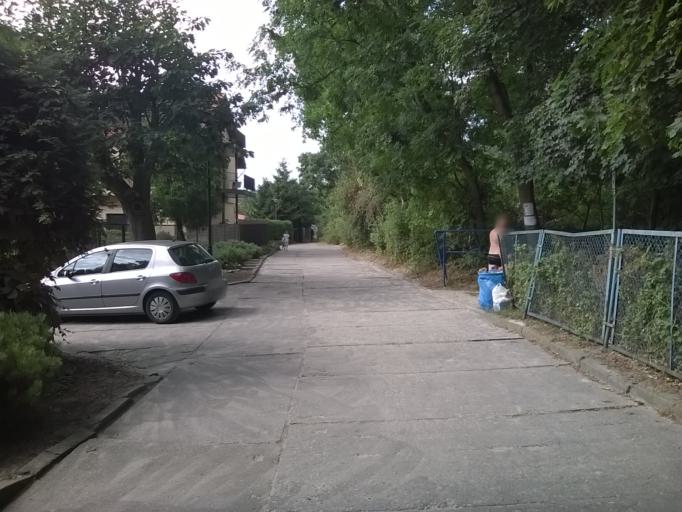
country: PL
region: West Pomeranian Voivodeship
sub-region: Powiat kolobrzeski
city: Ustronie Morskie
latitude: 54.2430
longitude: 15.8715
